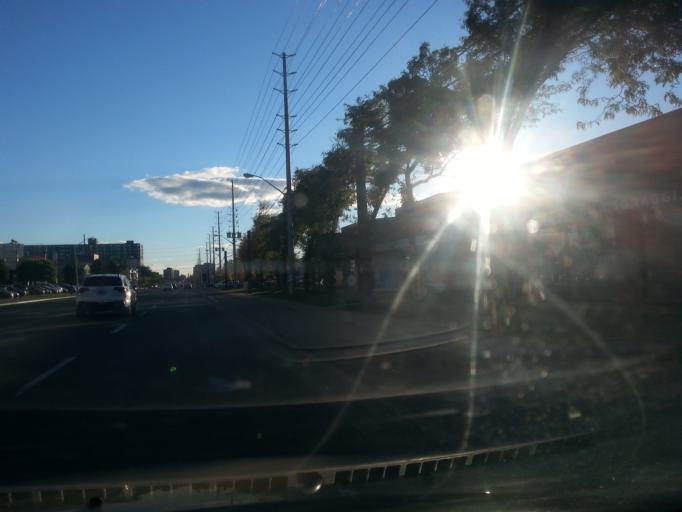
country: CA
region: Ontario
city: Mississauga
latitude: 43.5860
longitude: -79.6099
